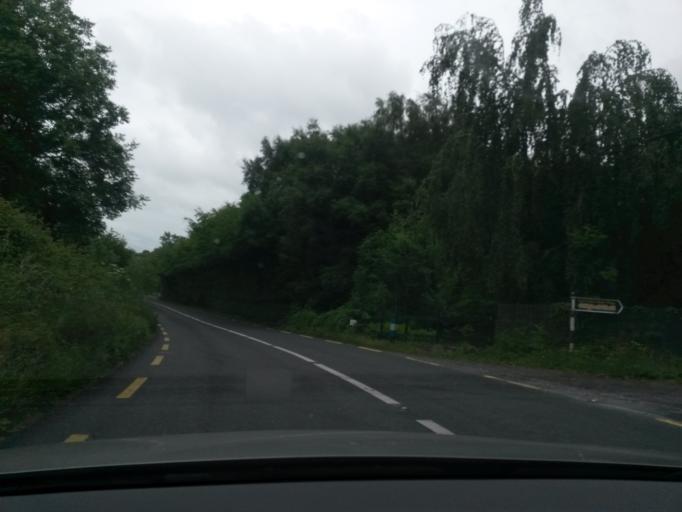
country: IE
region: Connaught
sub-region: Sligo
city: Strandhill
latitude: 54.2024
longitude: -8.5862
